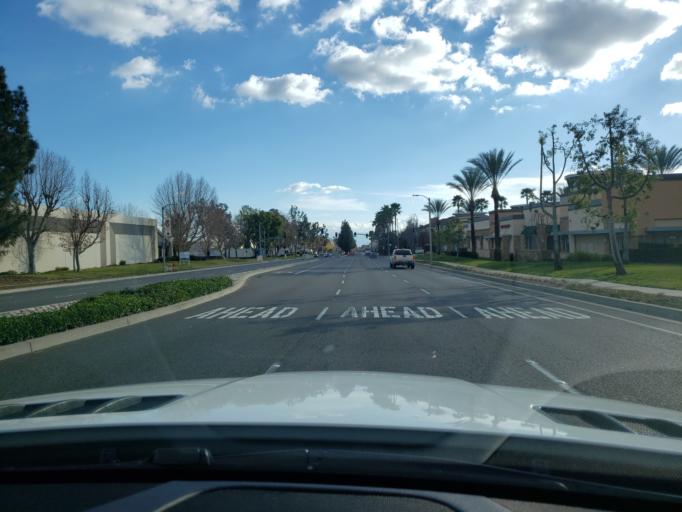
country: US
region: California
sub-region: San Bernardino County
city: Rancho Cucamonga
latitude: 34.0895
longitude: -117.5585
